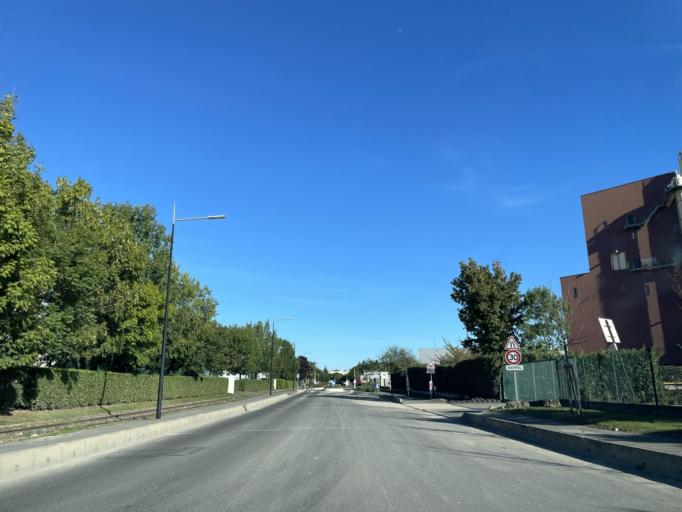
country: FR
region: Ile-de-France
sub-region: Departement du Val-de-Marne
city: Bonneuil-sur-Marne
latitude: 48.7798
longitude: 2.4885
